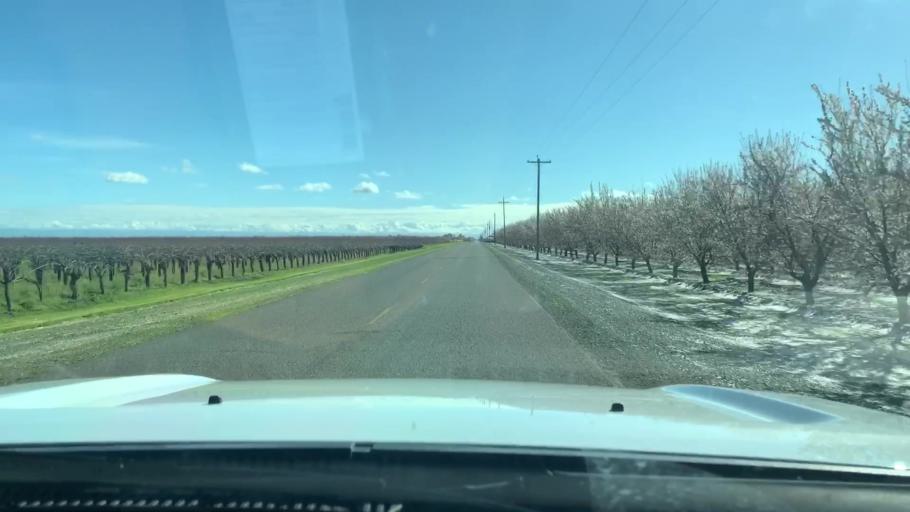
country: US
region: California
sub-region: Fresno County
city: Laton
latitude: 36.4894
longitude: -119.7299
